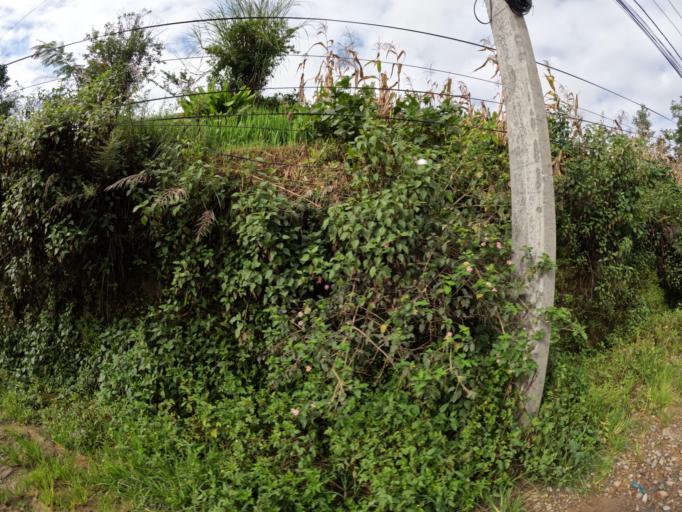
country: NP
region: Central Region
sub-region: Bagmati Zone
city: Kathmandu
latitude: 27.7669
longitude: 85.3323
